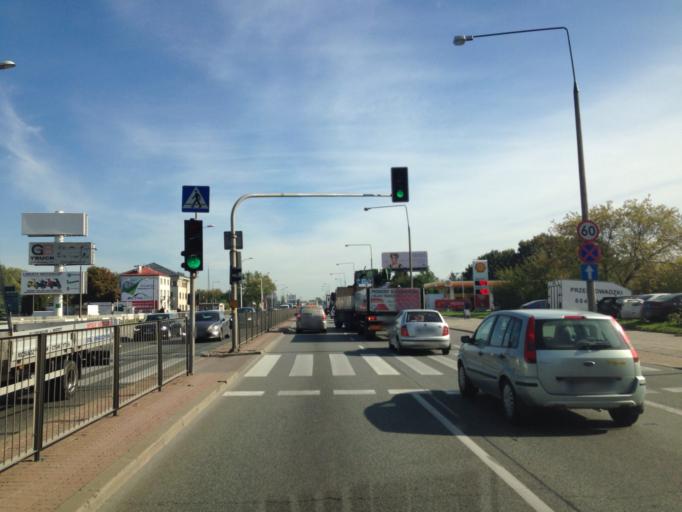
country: PL
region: Masovian Voivodeship
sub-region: Warszawa
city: Wlochy
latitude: 52.1932
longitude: 20.9430
